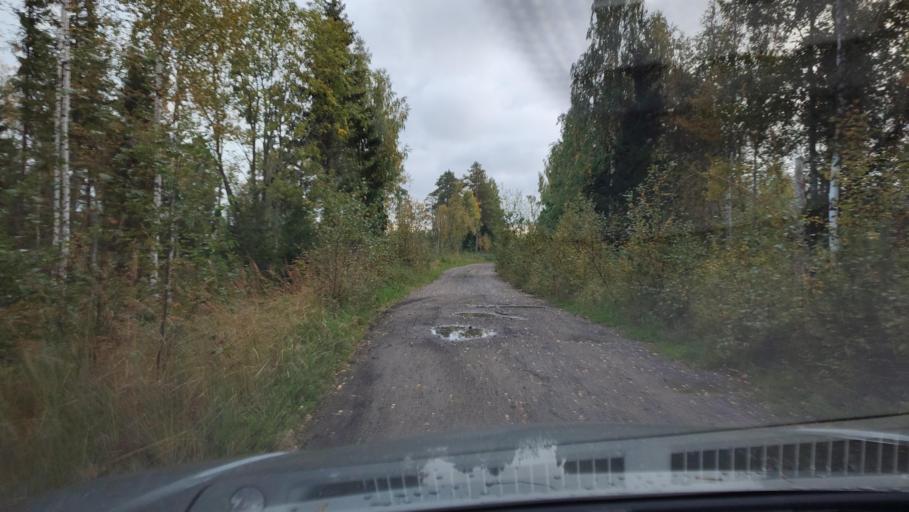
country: FI
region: Ostrobothnia
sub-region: Sydosterbotten
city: Kristinestad
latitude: 62.2705
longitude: 21.4337
